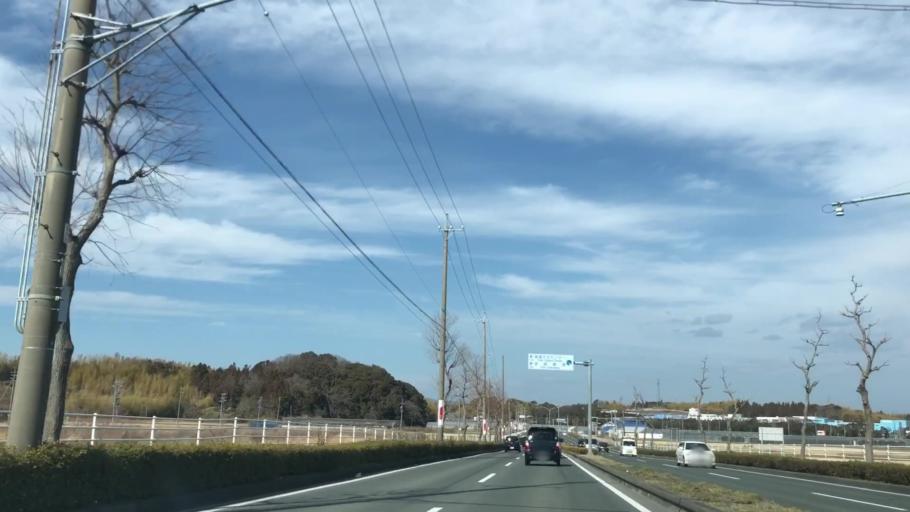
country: JP
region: Shizuoka
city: Hamamatsu
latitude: 34.7031
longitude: 137.6483
